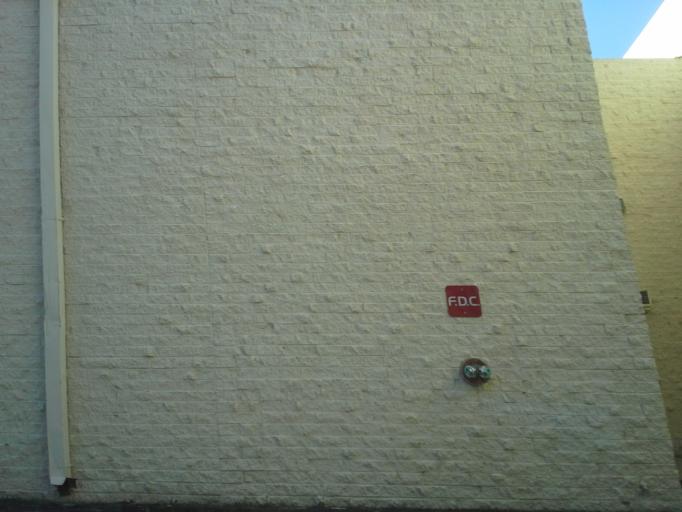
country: US
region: Arizona
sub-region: Maricopa County
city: Paradise Valley
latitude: 33.6128
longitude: -111.9792
